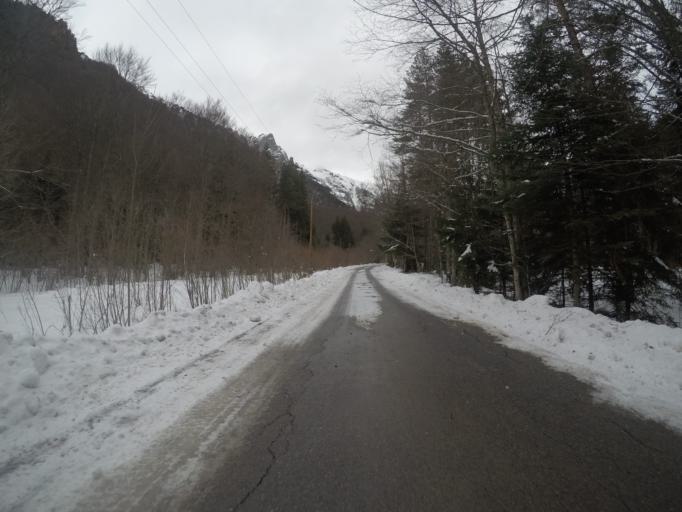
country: BG
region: Kyustendil
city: Sapareva Banya
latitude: 42.1479
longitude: 23.3703
